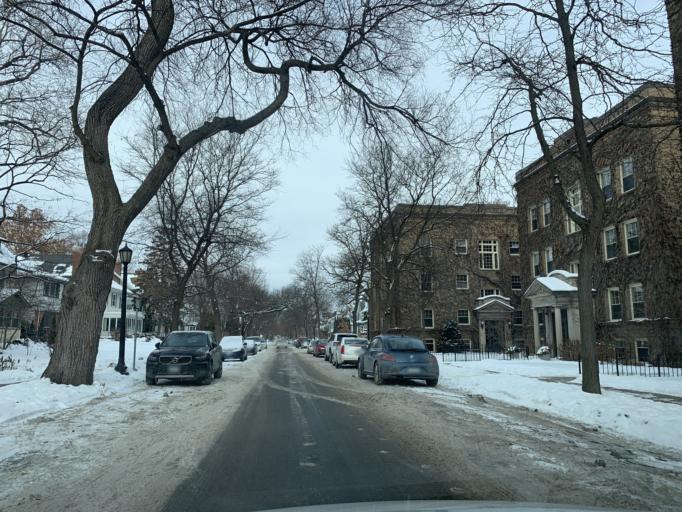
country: US
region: Minnesota
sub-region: Hennepin County
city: Minneapolis
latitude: 44.9561
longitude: -93.2982
